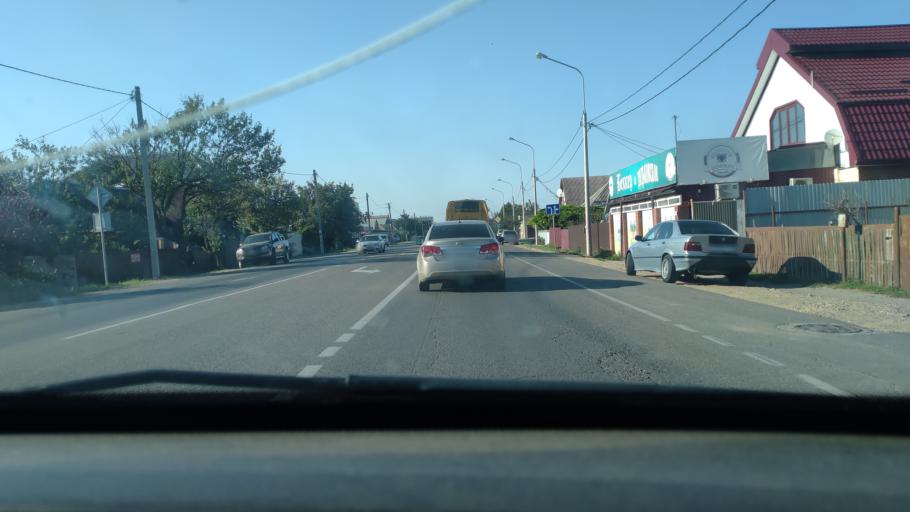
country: RU
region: Krasnodarskiy
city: Novotitarovskaya
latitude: 45.2464
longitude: 38.9968
